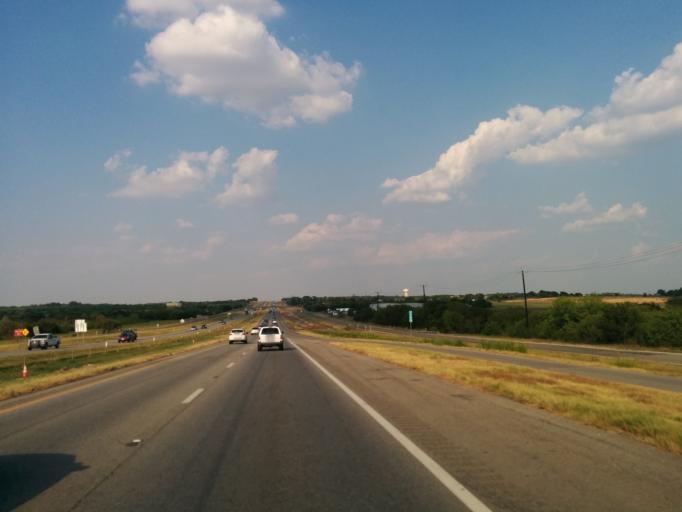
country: US
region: Texas
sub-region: Bexar County
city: Converse
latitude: 29.4781
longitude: -98.2520
